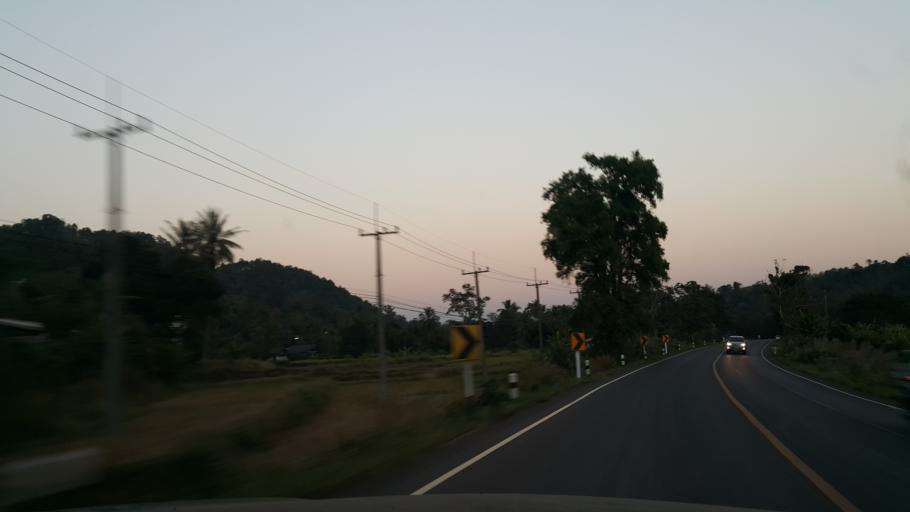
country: TH
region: Phrae
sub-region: Amphoe Wang Chin
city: Wang Chin
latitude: 17.9735
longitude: 99.6251
